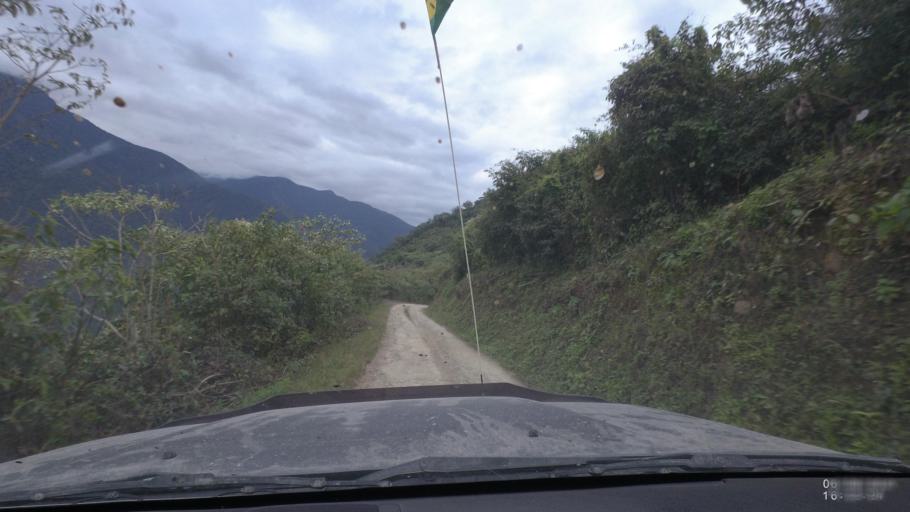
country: BO
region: La Paz
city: Quime
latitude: -16.5418
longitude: -66.7524
